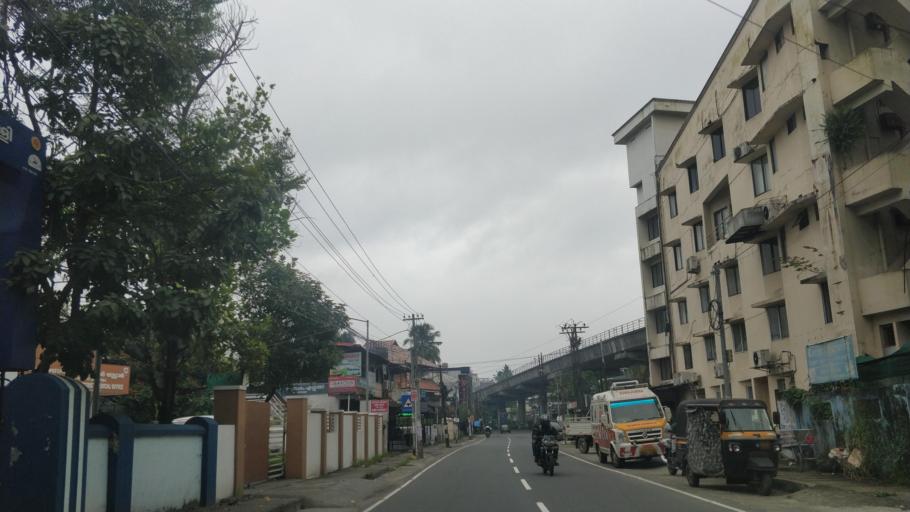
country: IN
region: Kerala
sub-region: Ernakulam
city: Elur
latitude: 10.0175
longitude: 76.3024
